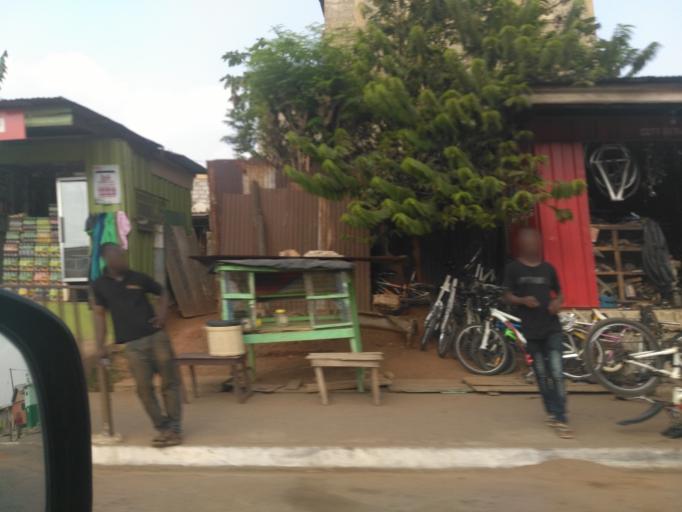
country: GH
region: Greater Accra
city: Accra
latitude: 5.5801
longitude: -0.1954
